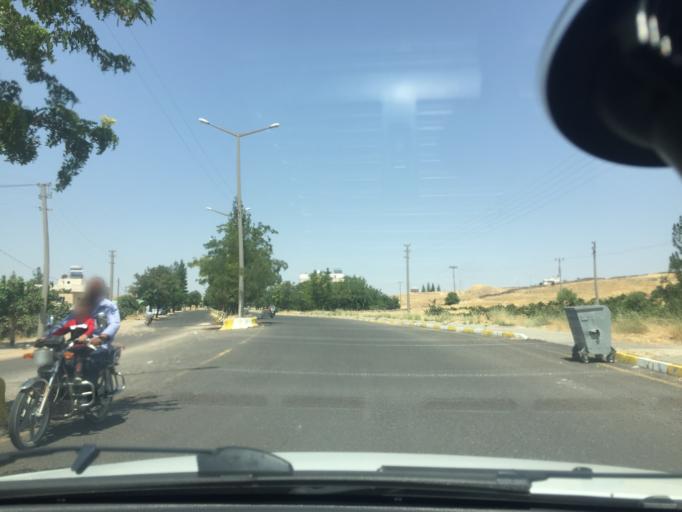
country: TR
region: Mardin
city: Kindirip
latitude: 37.4542
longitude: 41.2238
